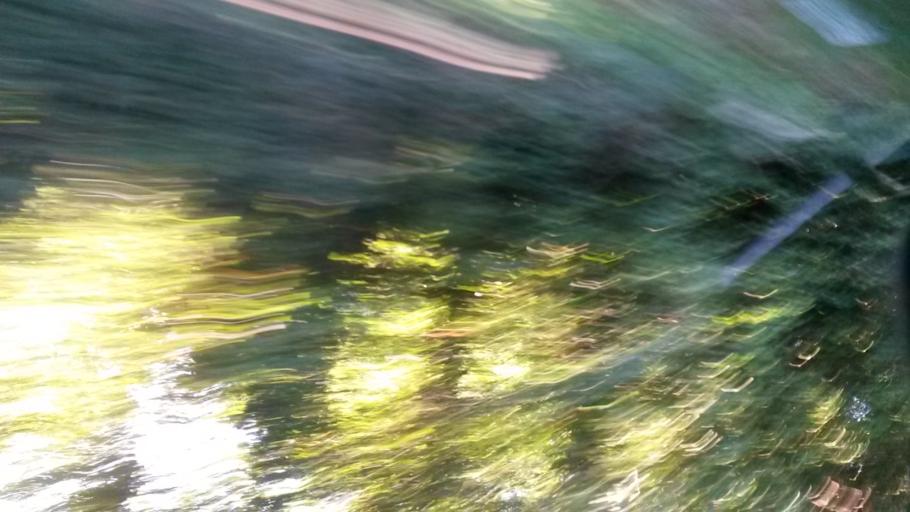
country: IE
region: Leinster
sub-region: An Mhi
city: Ashbourne
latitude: 53.4891
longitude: -6.3322
